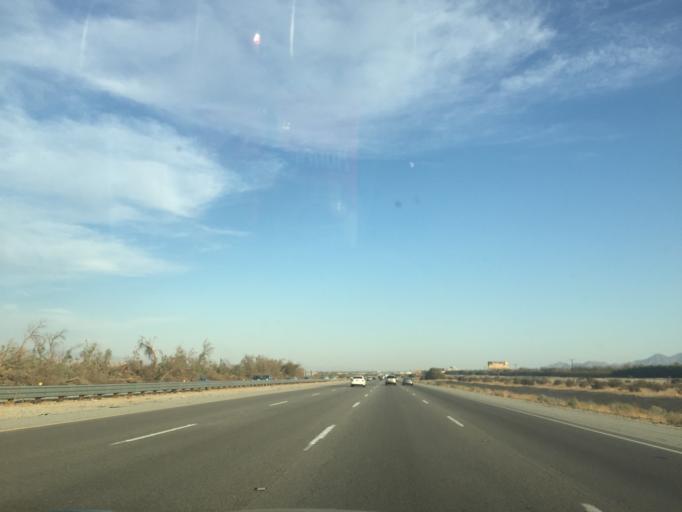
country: US
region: California
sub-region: Riverside County
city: Thousand Palms
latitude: 33.8417
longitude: -116.4461
